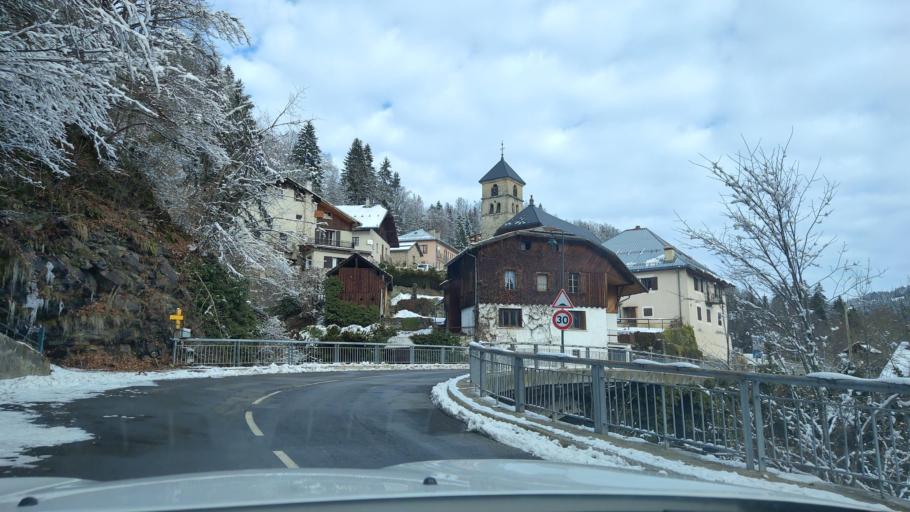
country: FR
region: Rhone-Alpes
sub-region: Departement de la Savoie
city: Ugine
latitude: 45.7721
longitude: 6.4724
